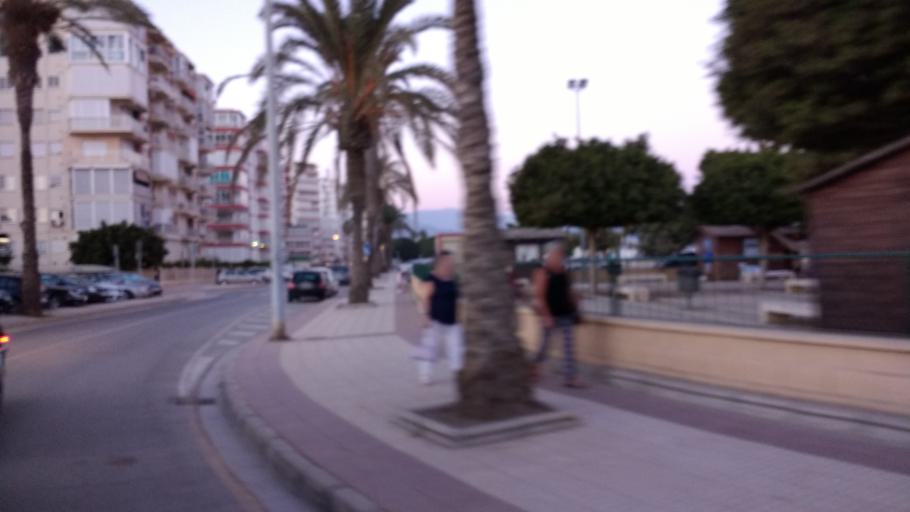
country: ES
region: Andalusia
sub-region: Provincia de Malaga
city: Velez-Malaga
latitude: 36.7332
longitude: -4.0985
